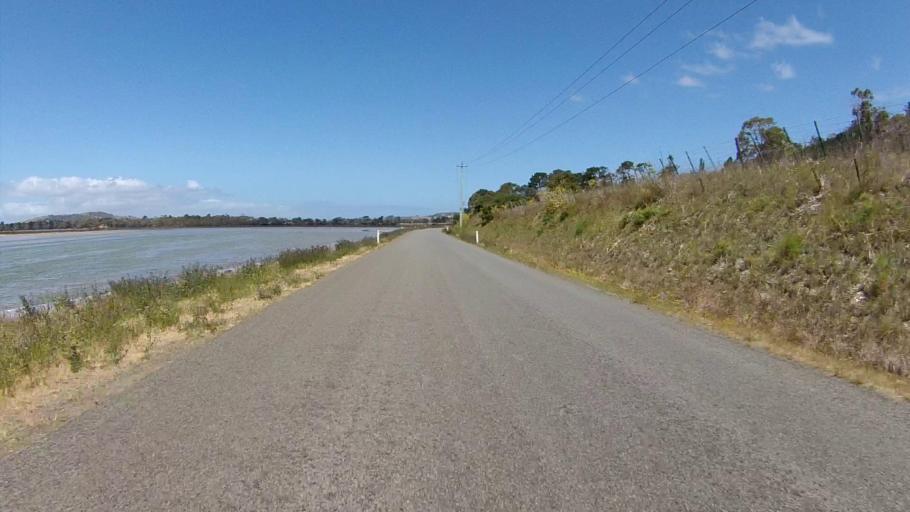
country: AU
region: Tasmania
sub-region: Clarence
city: Lauderdale
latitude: -42.9215
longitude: 147.4802
